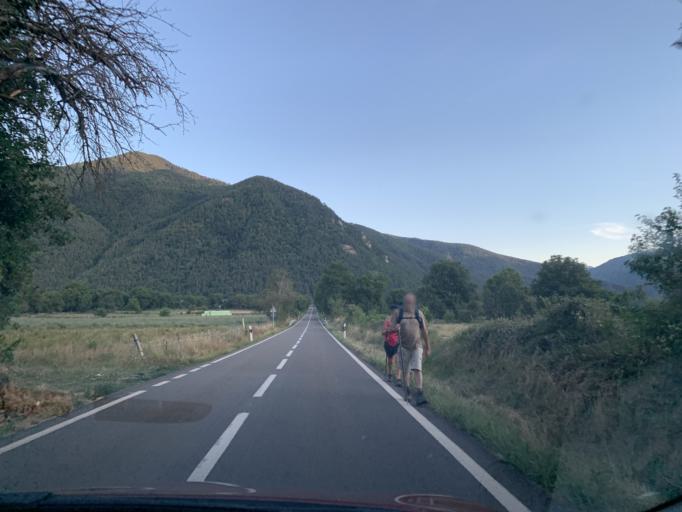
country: ES
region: Aragon
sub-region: Provincia de Huesca
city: Broto
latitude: 42.5759
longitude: -0.1133
